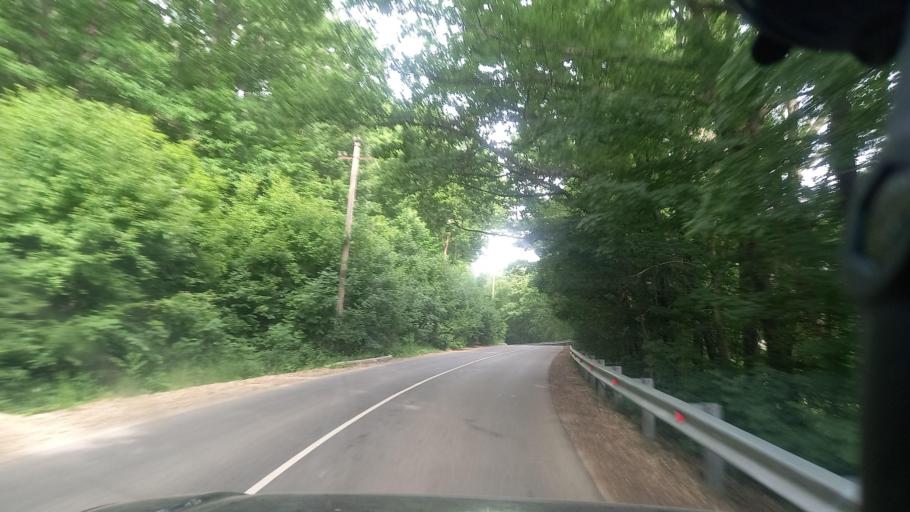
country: RU
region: Krasnodarskiy
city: Goryachiy Klyuch
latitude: 44.6043
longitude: 39.0032
